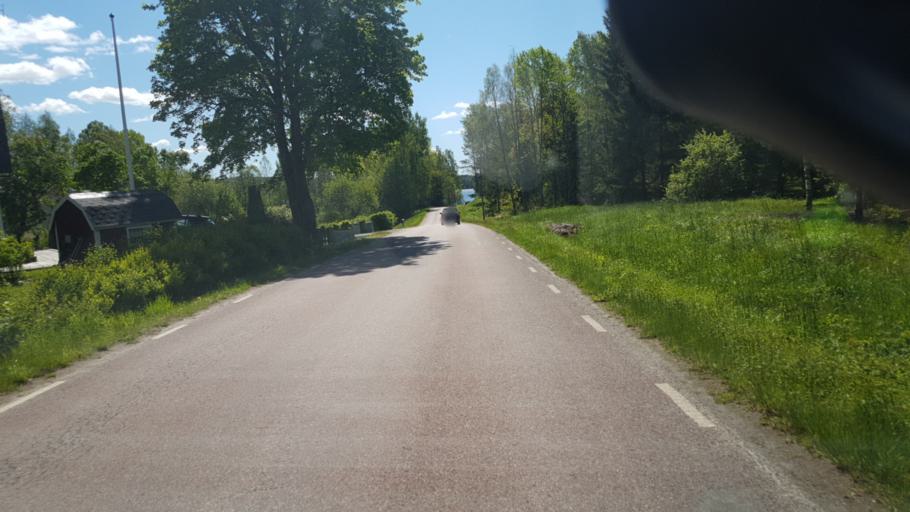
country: SE
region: Vaermland
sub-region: Grums Kommun
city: Slottsbron
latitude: 59.4564
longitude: 12.8824
